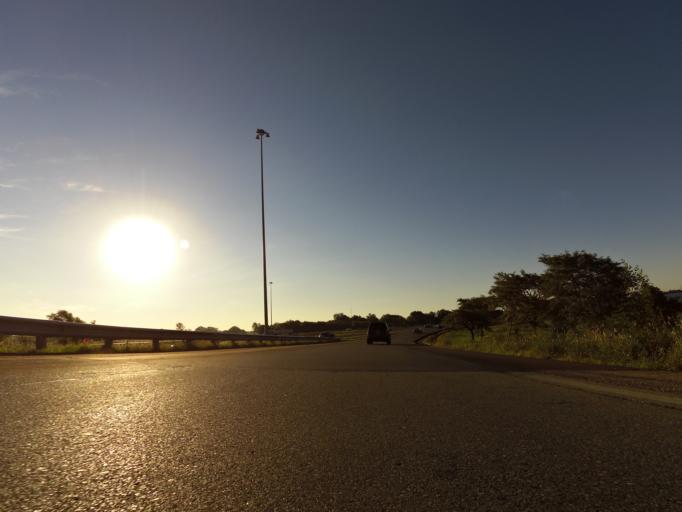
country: US
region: Kansas
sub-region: Sedgwick County
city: Park City
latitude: 37.7586
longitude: -97.3228
